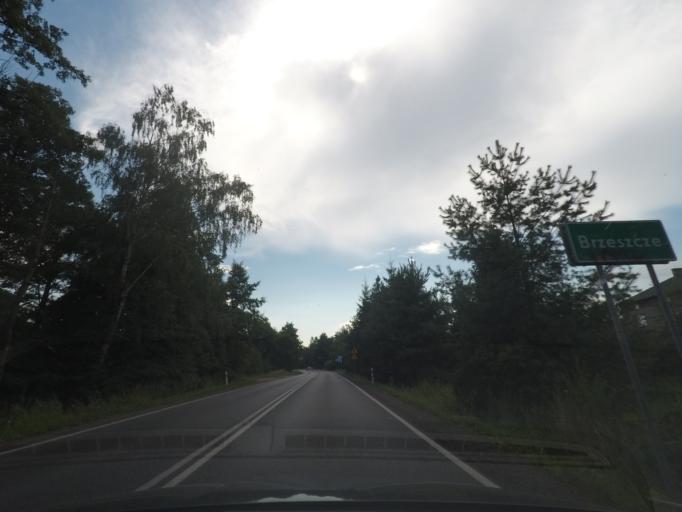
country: PL
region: Lesser Poland Voivodeship
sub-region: Powiat oswiecimski
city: Rajsko
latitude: 50.0028
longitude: 19.1770
